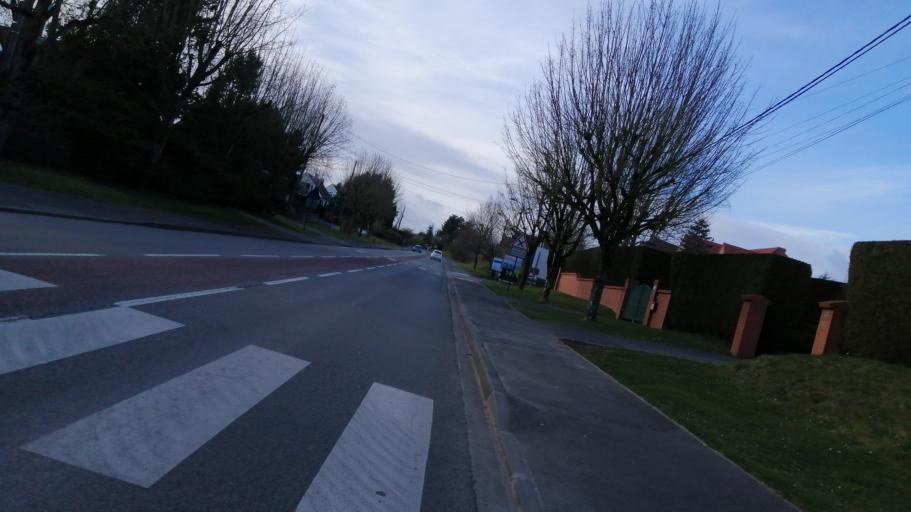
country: FR
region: Nord-Pas-de-Calais
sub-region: Departement du Pas-de-Calais
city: Beaurains
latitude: 50.2564
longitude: 2.8037
